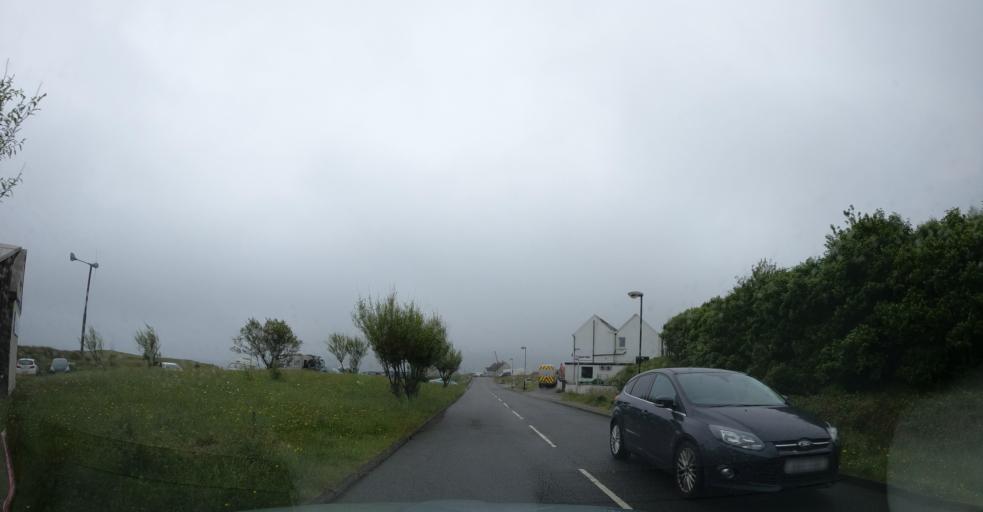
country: GB
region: Scotland
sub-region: Eilean Siar
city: Isle of North Uist
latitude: 57.5986
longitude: -7.1594
